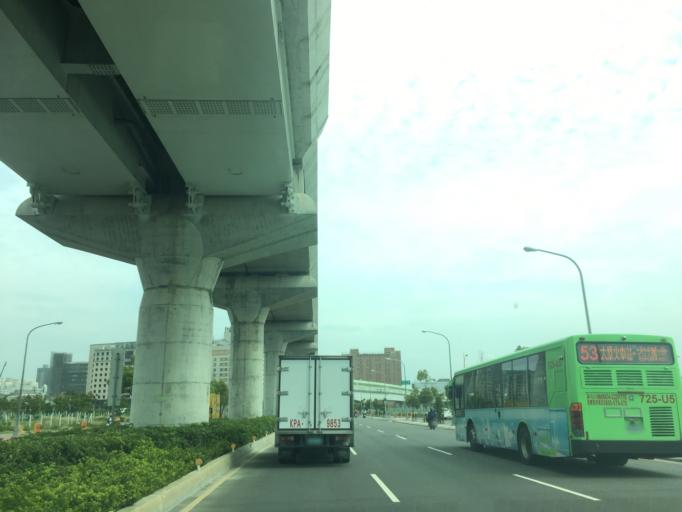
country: TW
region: Taiwan
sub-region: Taichung City
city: Taichung
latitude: 24.1255
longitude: 120.6465
